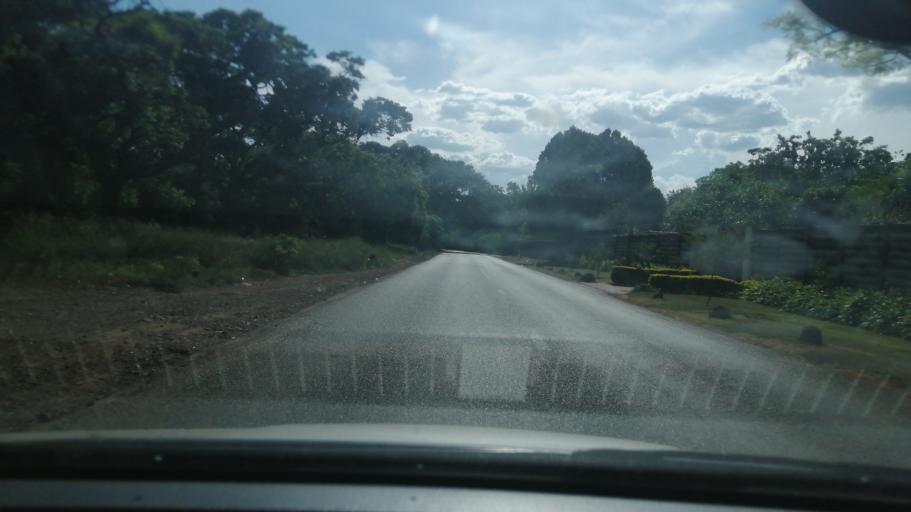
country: ZW
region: Harare
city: Harare
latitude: -17.7954
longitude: 31.0541
